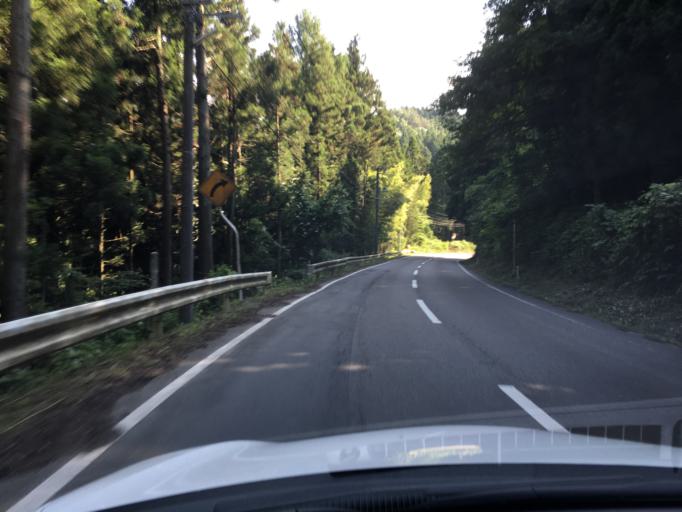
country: JP
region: Fukushima
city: Ishikawa
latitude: 37.2115
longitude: 140.5409
